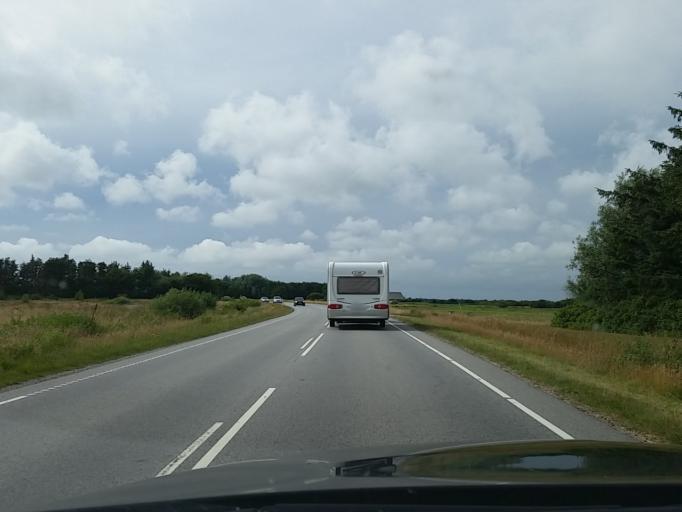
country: DK
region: South Denmark
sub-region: Varde Kommune
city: Oksbol
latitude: 55.7851
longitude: 8.2633
